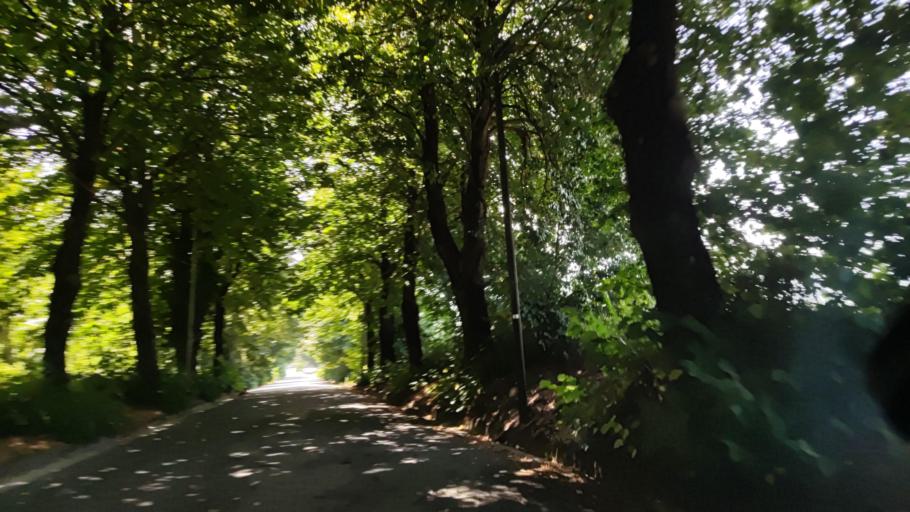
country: IT
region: Calabria
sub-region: Provincia di Reggio Calabria
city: Seminara
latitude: 38.3352
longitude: 15.8463
